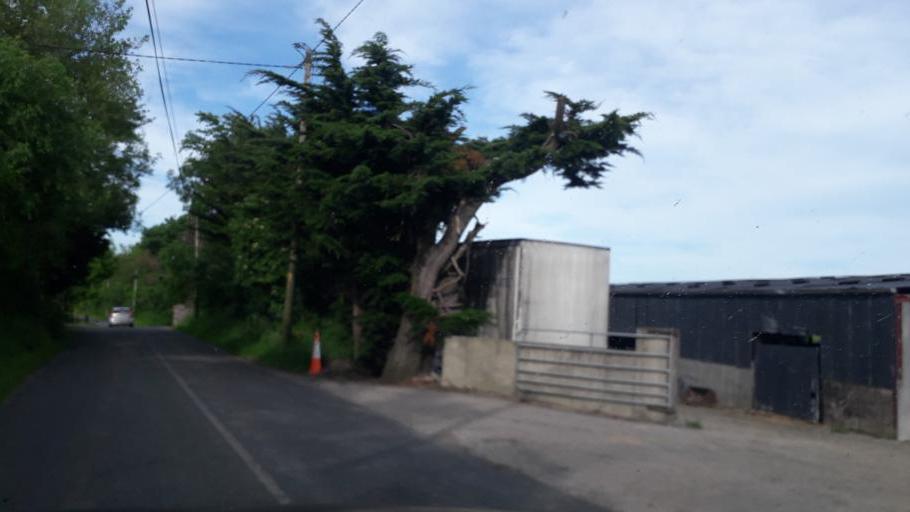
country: IE
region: Leinster
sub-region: Loch Garman
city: Courtown
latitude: 52.5547
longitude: -6.2403
